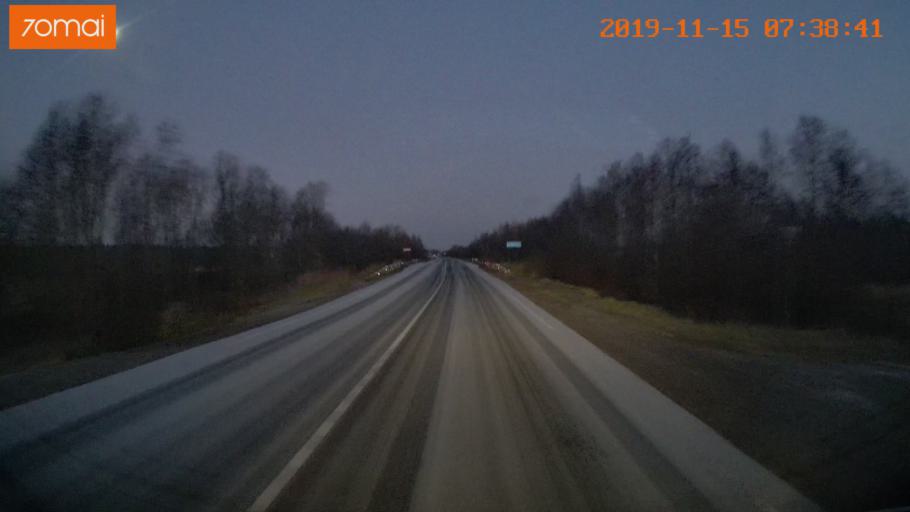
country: RU
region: Vologda
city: Sheksna
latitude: 58.7594
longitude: 38.3973
